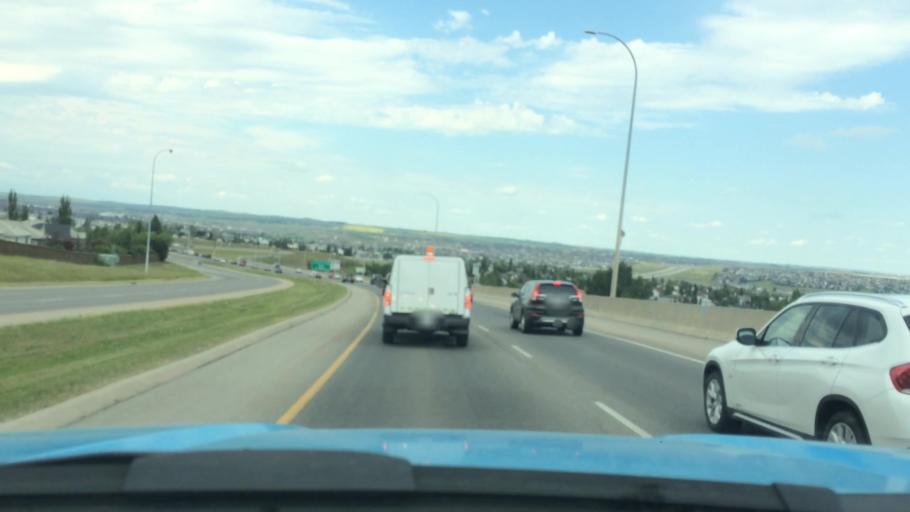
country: CA
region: Alberta
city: Calgary
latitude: 51.1377
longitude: -114.1209
